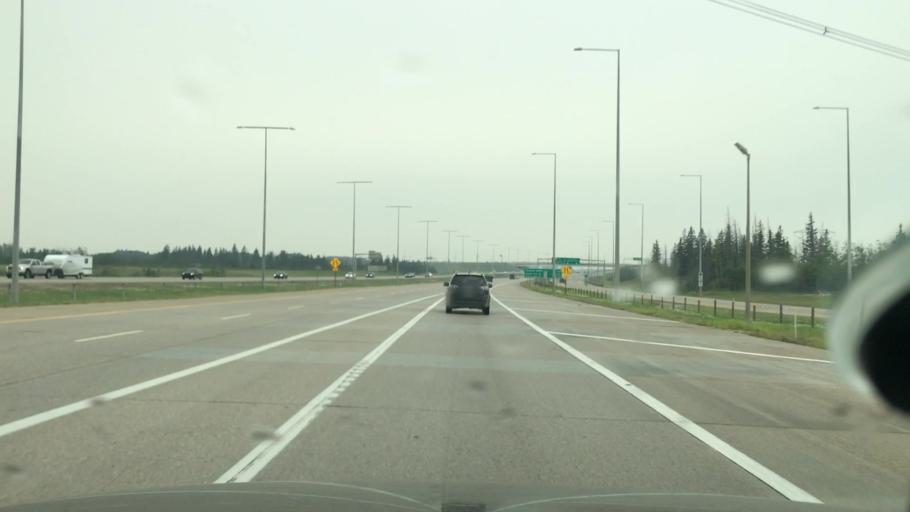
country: CA
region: Alberta
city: Edmonton
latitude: 53.4357
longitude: -113.5054
